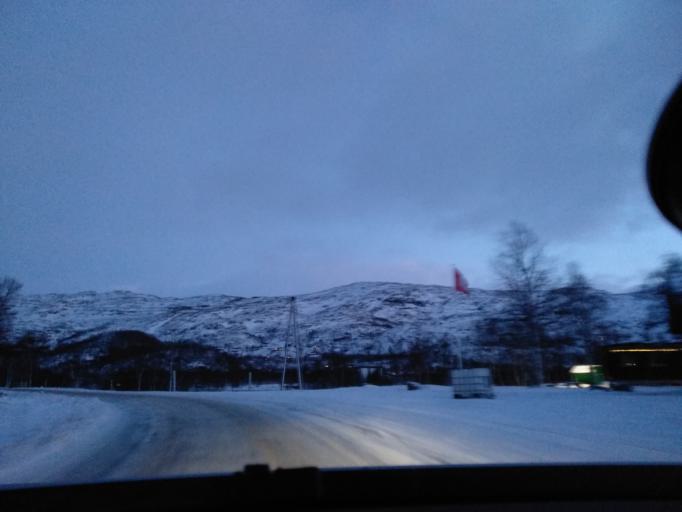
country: NO
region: Vest-Agder
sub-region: Sirdal
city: Tonstad
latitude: 59.0181
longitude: 6.9307
